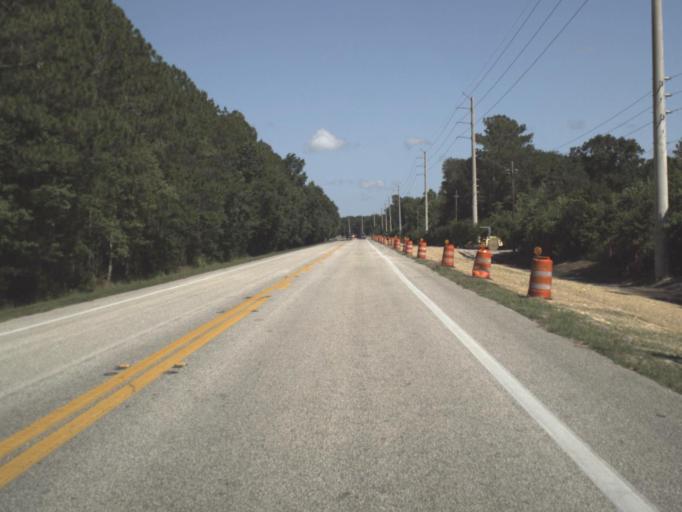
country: US
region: Florida
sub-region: Saint Johns County
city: Saint Augustine
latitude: 29.9559
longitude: -81.4599
